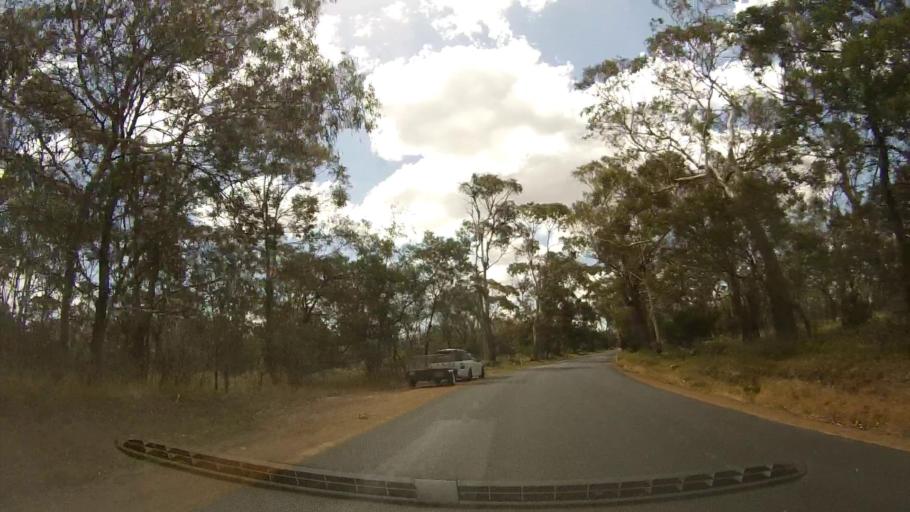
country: AU
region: Tasmania
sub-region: Clarence
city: Seven Mile Beach
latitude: -42.8276
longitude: 147.5080
